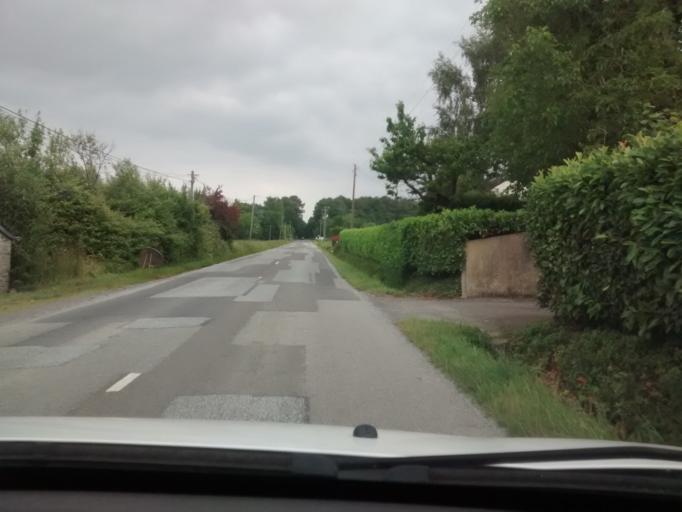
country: FR
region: Brittany
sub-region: Departement d'Ille-et-Vilaine
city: Servon-sur-Vilaine
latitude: 48.1381
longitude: -1.4533
